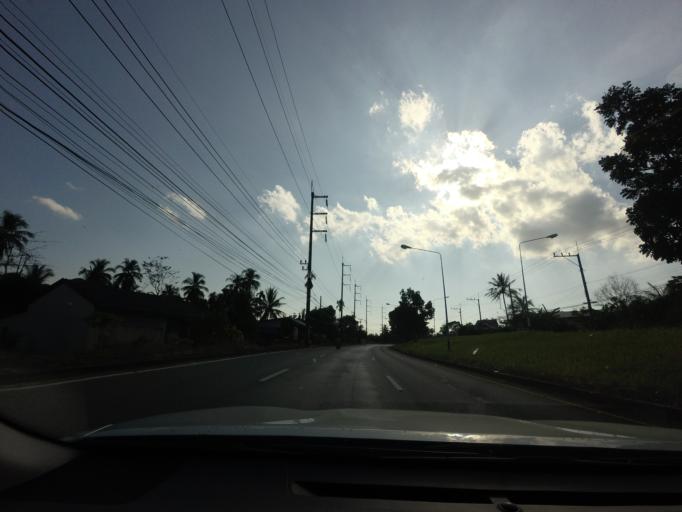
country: TH
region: Phangnga
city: Thai Mueang
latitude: 8.2713
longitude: 98.3221
